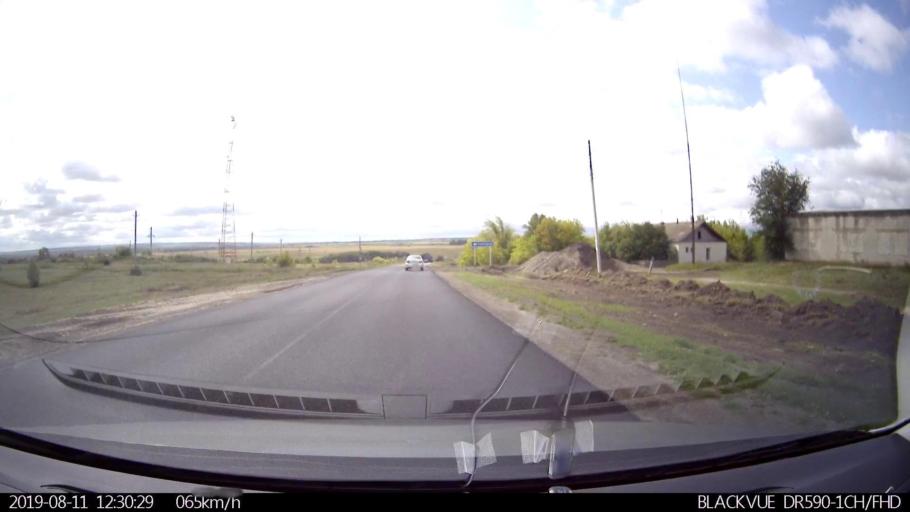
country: RU
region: Ulyanovsk
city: Ignatovka
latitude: 53.8254
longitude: 47.8938
